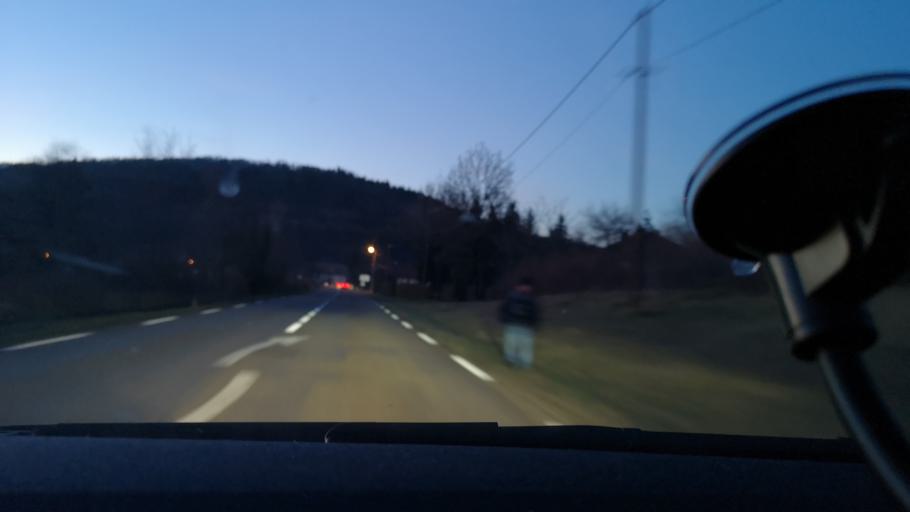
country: FR
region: Franche-Comte
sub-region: Departement du Jura
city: Champagnole
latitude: 46.7575
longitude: 5.9444
